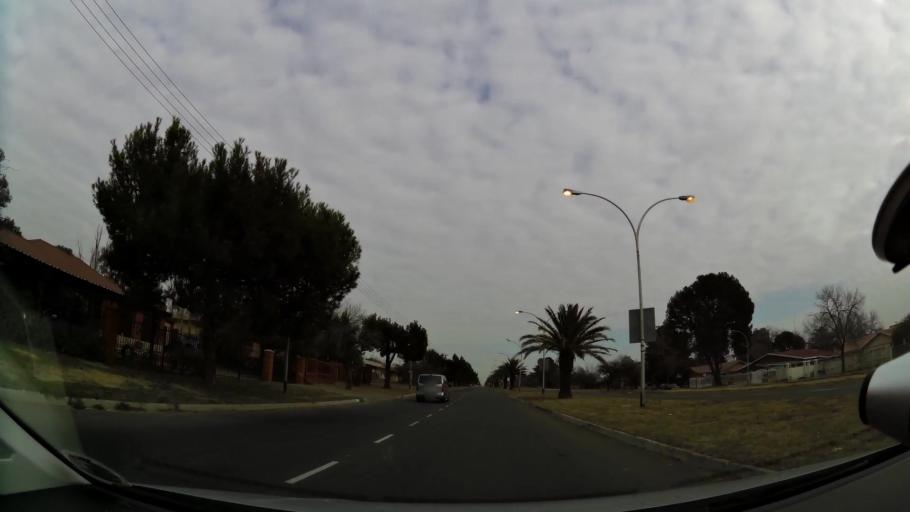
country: ZA
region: Orange Free State
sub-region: Mangaung Metropolitan Municipality
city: Bloemfontein
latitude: -29.1263
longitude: 26.1823
